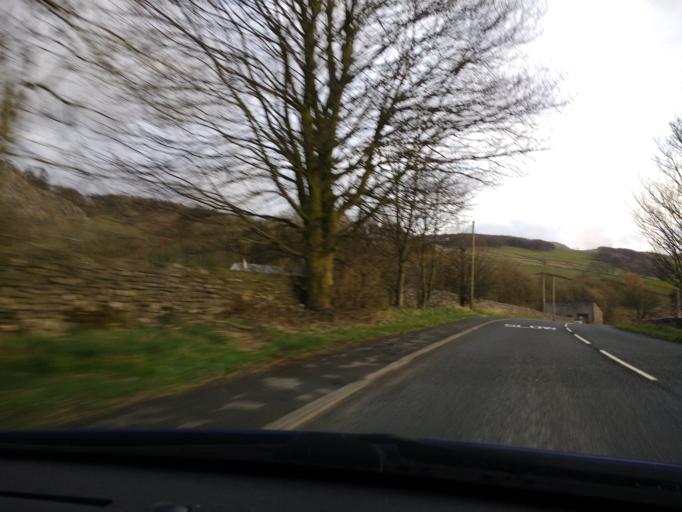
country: GB
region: England
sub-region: North Yorkshire
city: Settle
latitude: 54.0923
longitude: -2.2730
